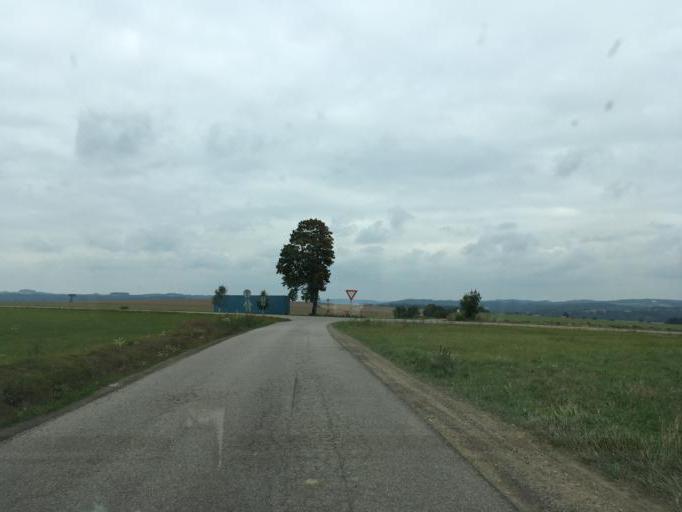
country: CZ
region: Central Bohemia
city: Vlasim
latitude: 49.7245
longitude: 14.8872
